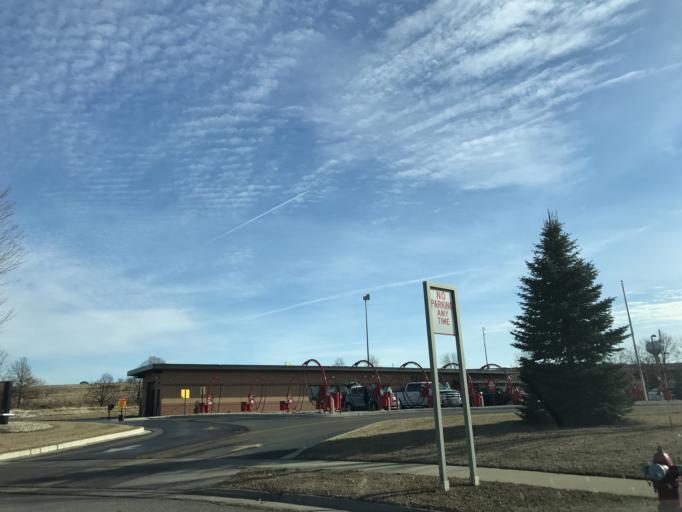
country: US
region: Wisconsin
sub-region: Dane County
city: Sun Prairie
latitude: 43.1473
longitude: -89.2875
